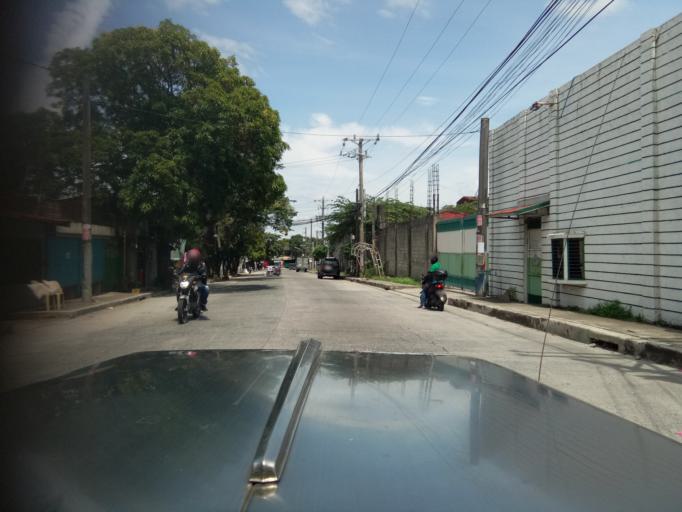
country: PH
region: Calabarzon
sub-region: Province of Cavite
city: Bulihan
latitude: 14.2876
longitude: 120.9980
